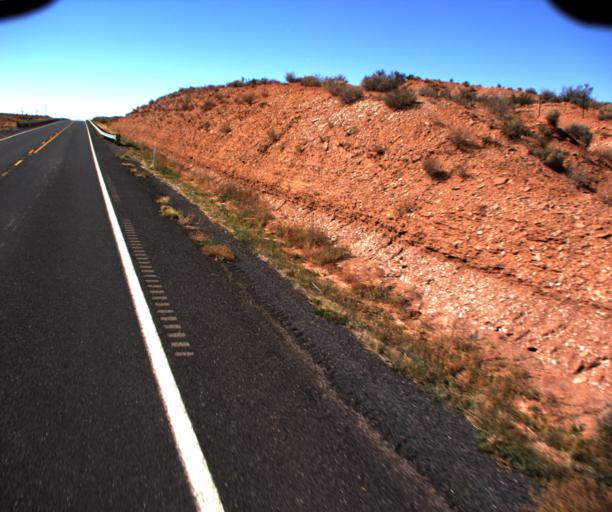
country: US
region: Arizona
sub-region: Coconino County
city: Fredonia
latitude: 36.9082
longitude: -112.5899
